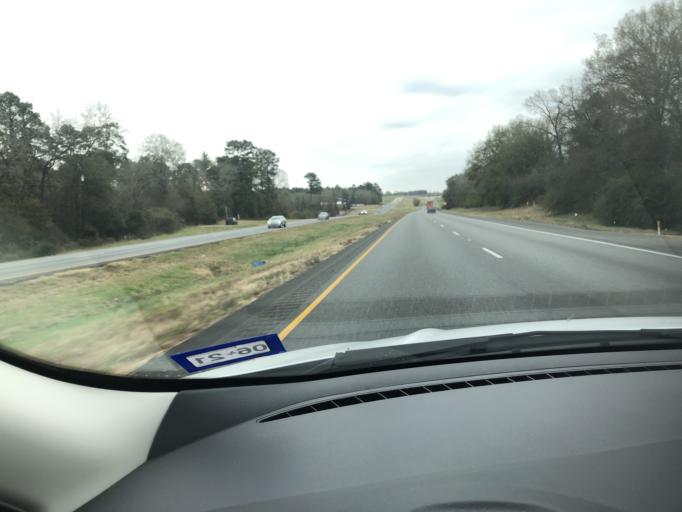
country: US
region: Texas
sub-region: Angelina County
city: Redland
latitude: 31.4238
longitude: -94.7247
